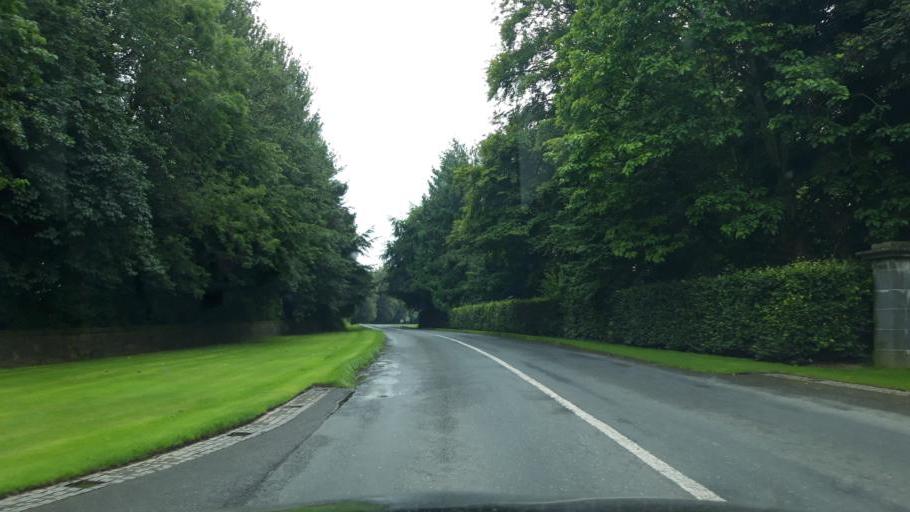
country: IE
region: Munster
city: Fethard
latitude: 52.5067
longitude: -7.6860
